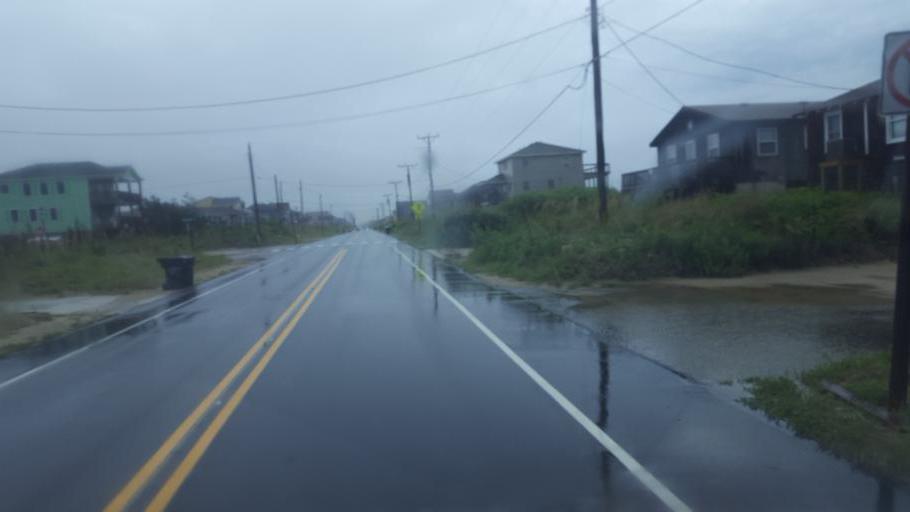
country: US
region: North Carolina
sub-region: Dare County
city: Kill Devil Hills
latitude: 36.0476
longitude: -75.6777
